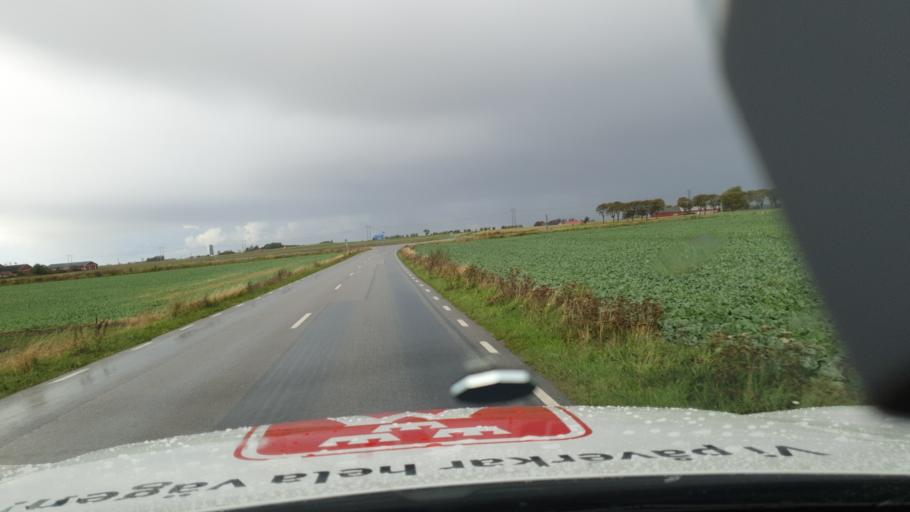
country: SE
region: Skane
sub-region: Malmo
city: Tygelsjo
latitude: 55.5146
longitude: 13.0204
